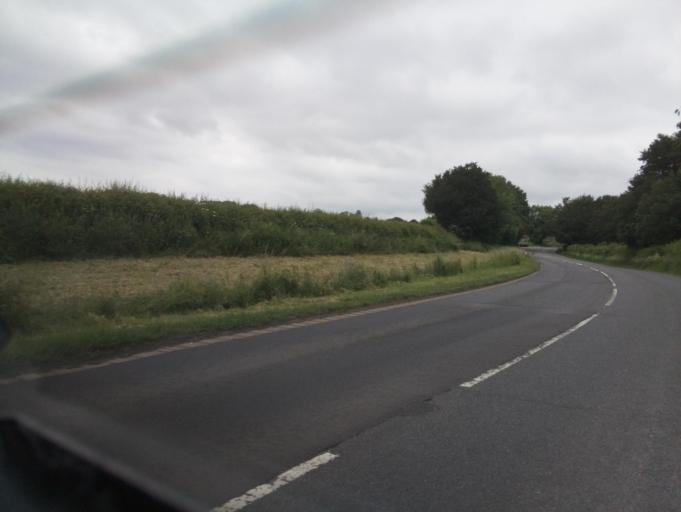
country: GB
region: England
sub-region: District of Rutland
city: Edith Weston
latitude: 52.6426
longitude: -0.6246
